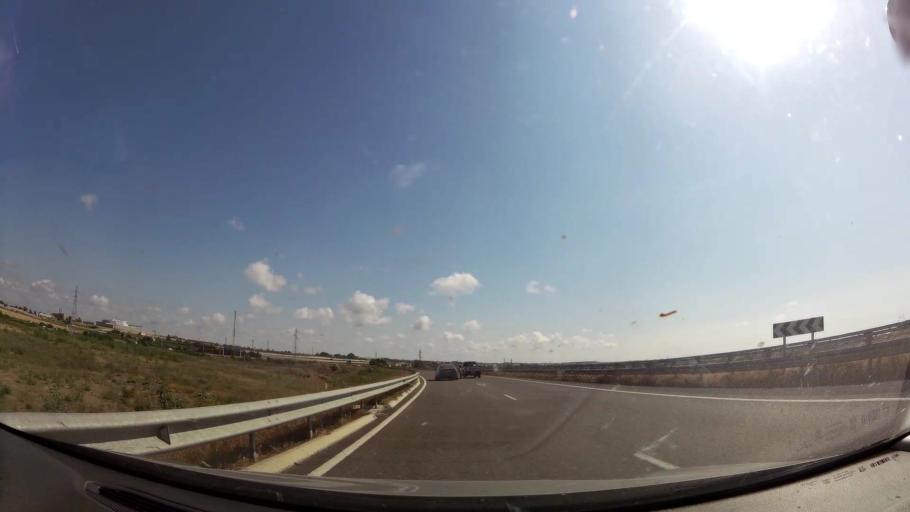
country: MA
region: Rabat-Sale-Zemmour-Zaer
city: Skhirat
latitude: 33.8747
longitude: -7.0143
